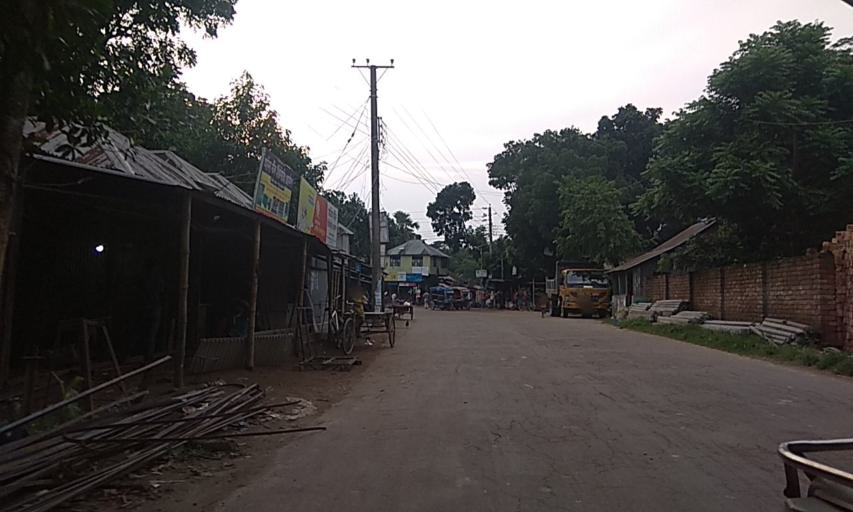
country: BD
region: Dhaka
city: Dohar
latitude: 23.4622
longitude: 89.9955
